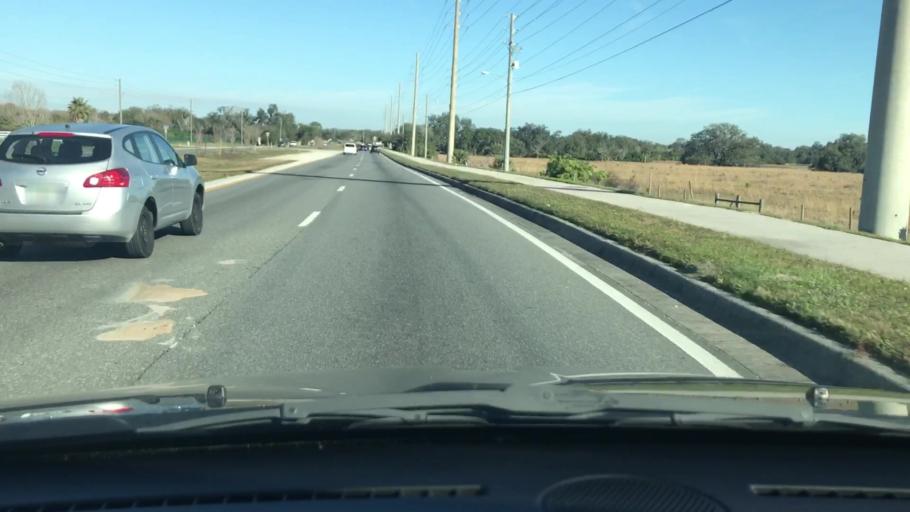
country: US
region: Florida
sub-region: Osceola County
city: Campbell
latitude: 28.2358
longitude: -81.4340
